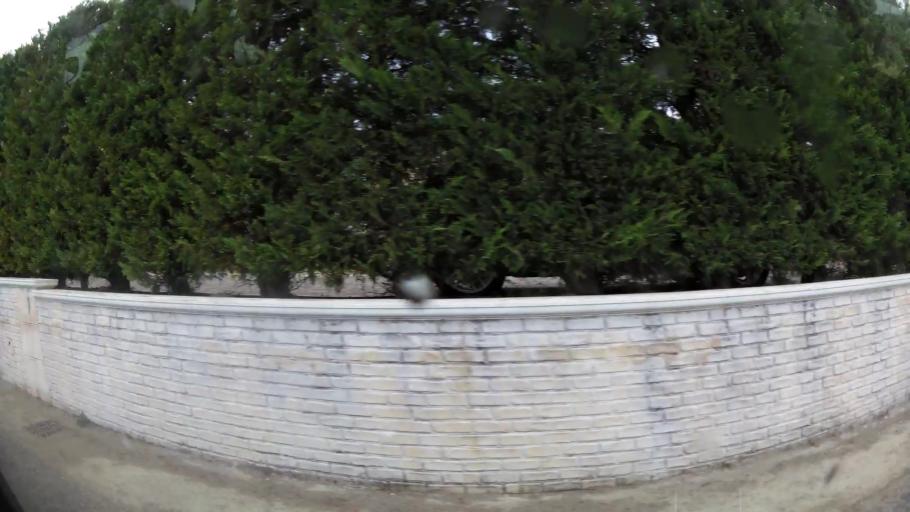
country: GR
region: Central Macedonia
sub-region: Nomos Pierias
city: Paralia
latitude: 40.2876
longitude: 22.6067
